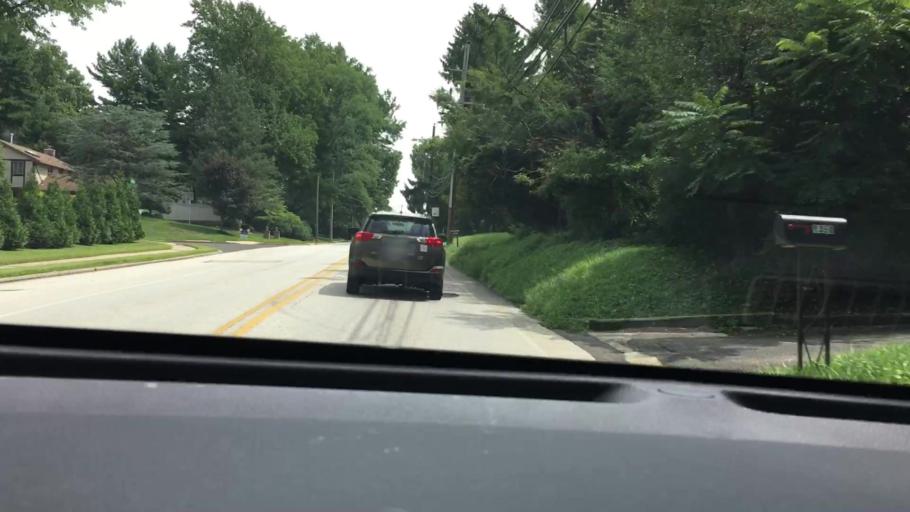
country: US
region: Pennsylvania
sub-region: Montgomery County
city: Bryn Athyn
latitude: 40.1526
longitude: -75.0641
